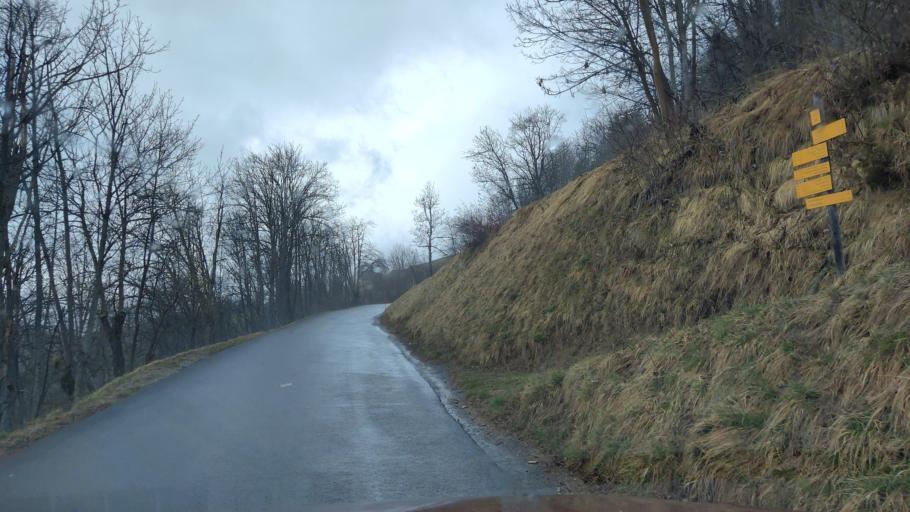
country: FR
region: Rhone-Alpes
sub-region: Departement de la Savoie
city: Saint-Jean-de-Maurienne
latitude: 45.1972
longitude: 6.2881
